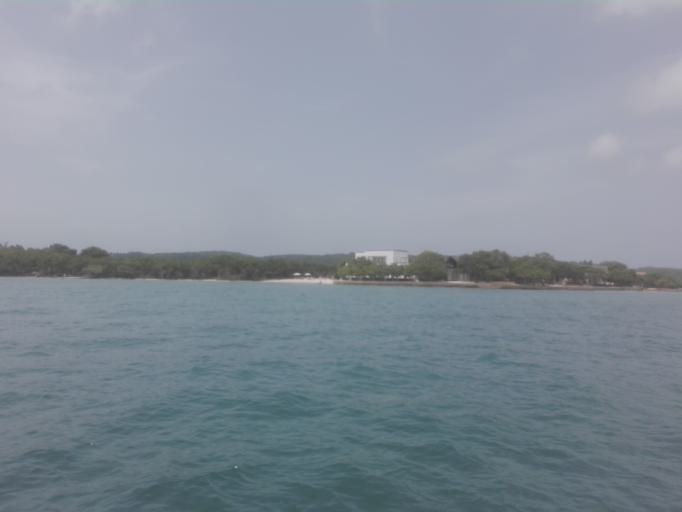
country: CO
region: Bolivar
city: Turbana
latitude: 10.1702
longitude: -75.6675
